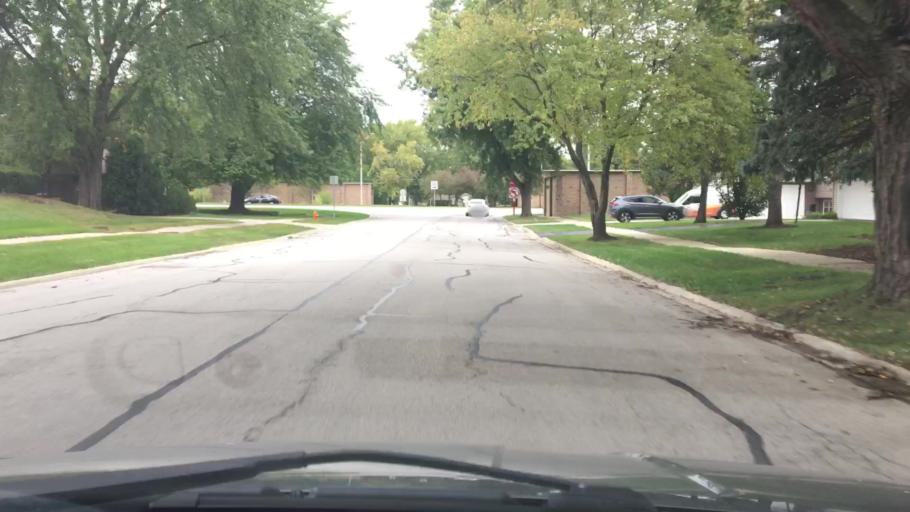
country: US
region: Illinois
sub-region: DuPage County
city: Naperville
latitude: 41.7474
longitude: -88.1350
